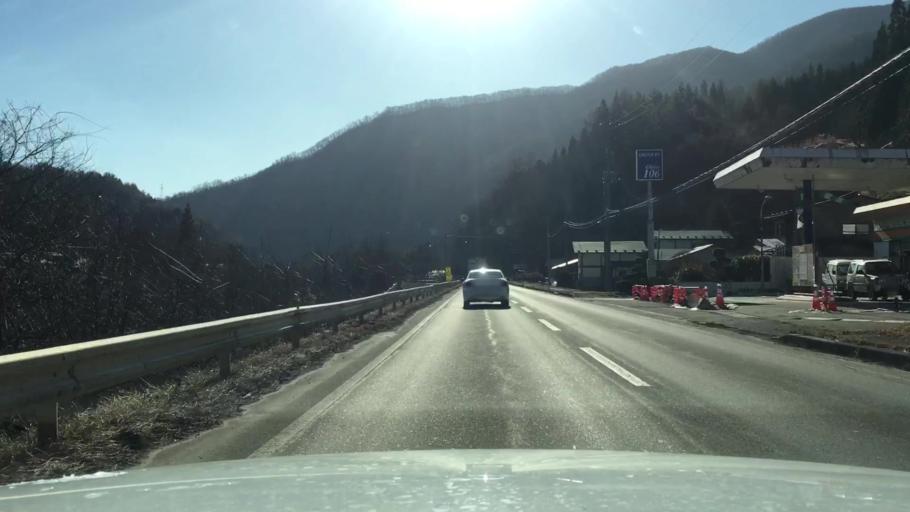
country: JP
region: Iwate
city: Tono
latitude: 39.6175
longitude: 141.6240
